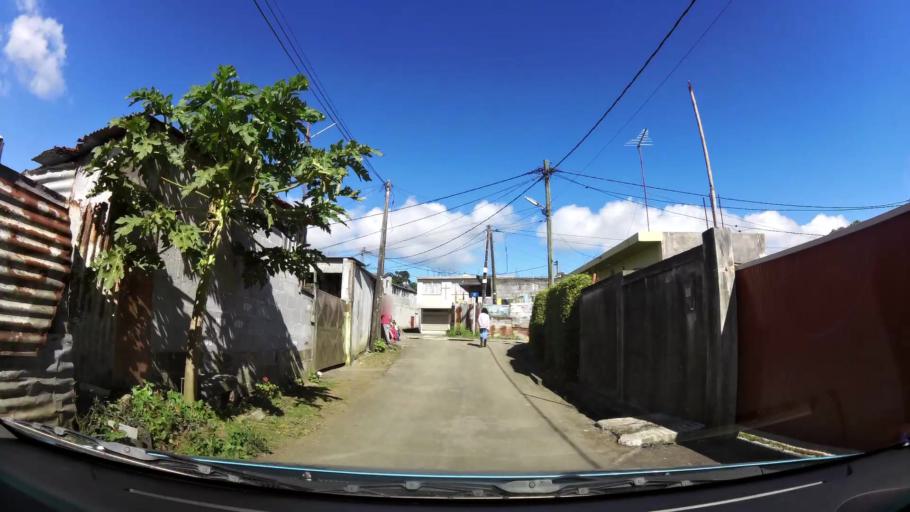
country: MU
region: Plaines Wilhems
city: Curepipe
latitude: -20.3046
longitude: 57.5025
